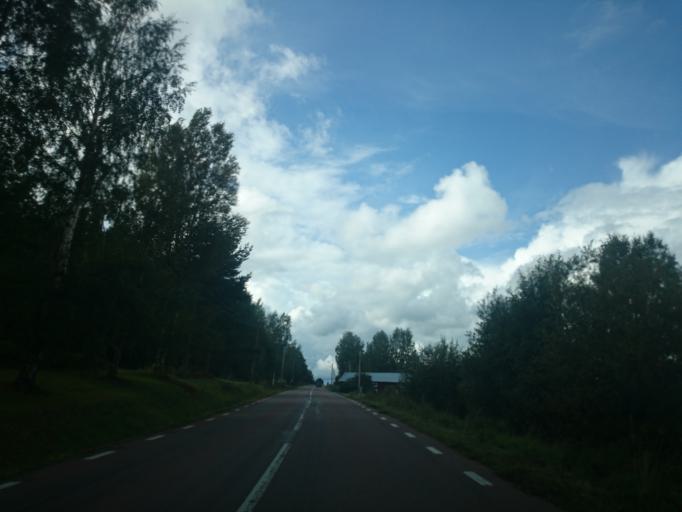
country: SE
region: Vaesternorrland
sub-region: Ange Kommun
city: Fransta
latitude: 62.4060
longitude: 16.5639
